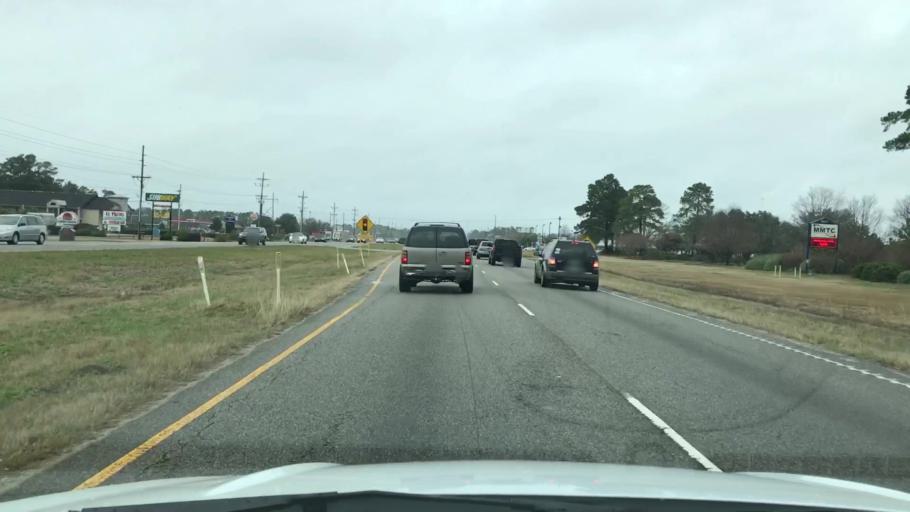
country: US
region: South Carolina
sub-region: Horry County
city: Red Hill
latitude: 33.7877
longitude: -78.9941
